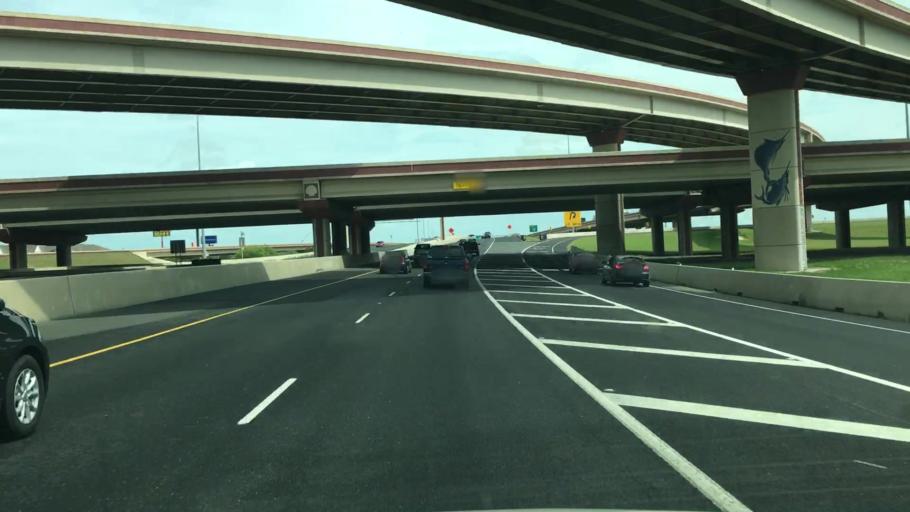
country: US
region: Texas
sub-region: Nueces County
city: Corpus Christi
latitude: 27.7375
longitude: -97.4313
